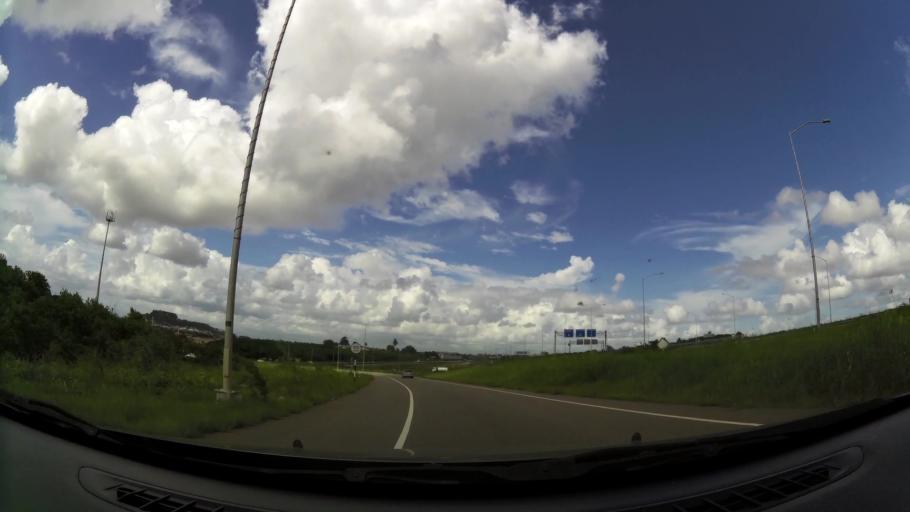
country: TT
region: City of San Fernando
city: Mon Repos
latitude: 10.2514
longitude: -61.4411
